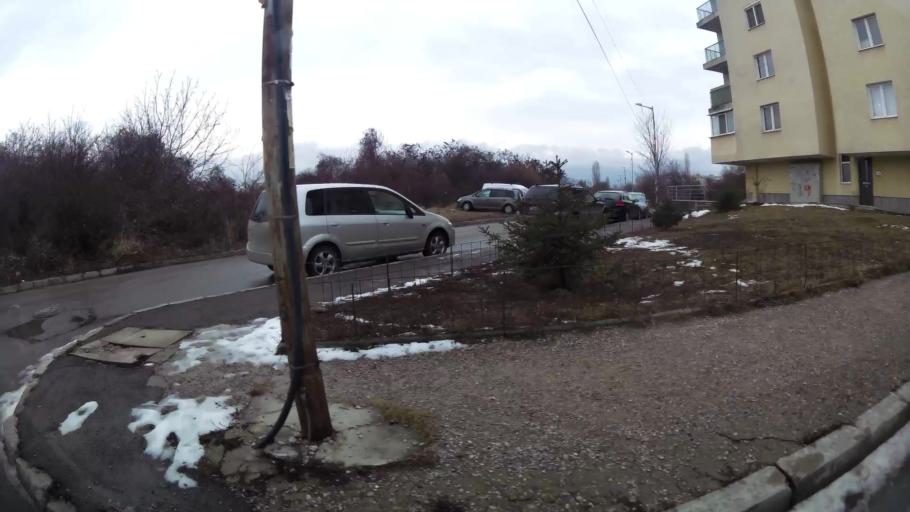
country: BG
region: Sofiya
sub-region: Obshtina Bozhurishte
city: Bozhurishte
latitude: 42.7271
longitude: 23.2574
